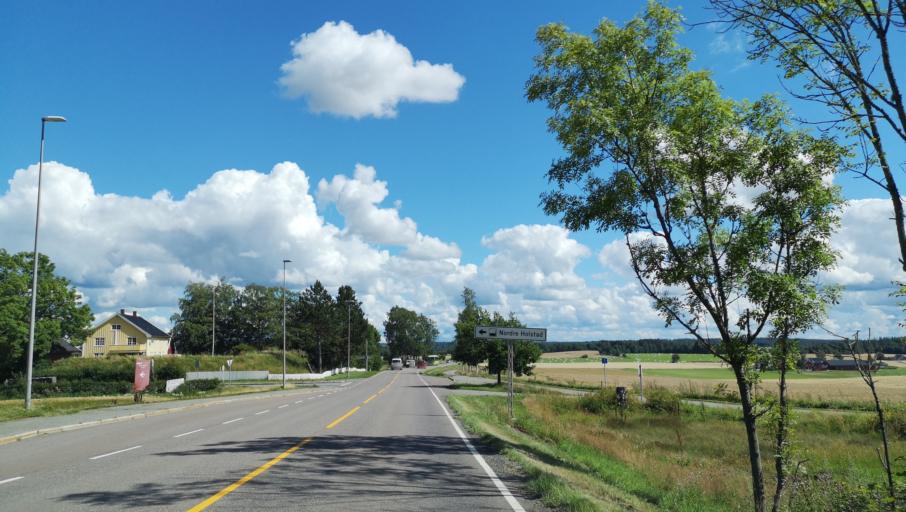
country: NO
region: Akershus
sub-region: Vestby
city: Vestby
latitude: 59.6585
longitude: 10.7139
